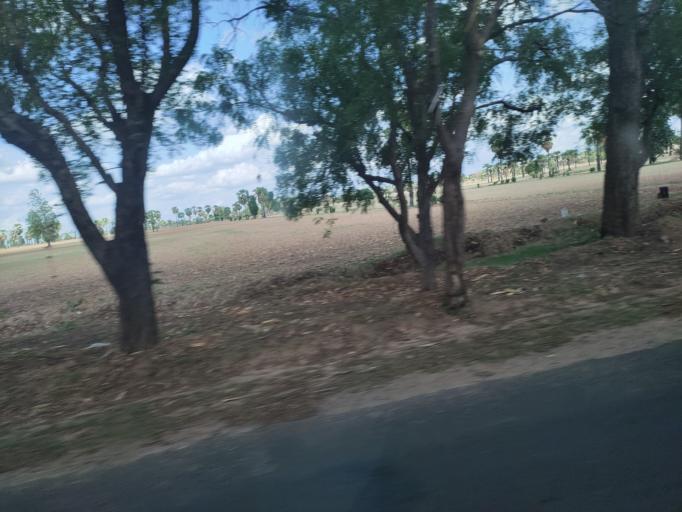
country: MM
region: Magway
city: Magway
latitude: 20.2162
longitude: 95.0175
